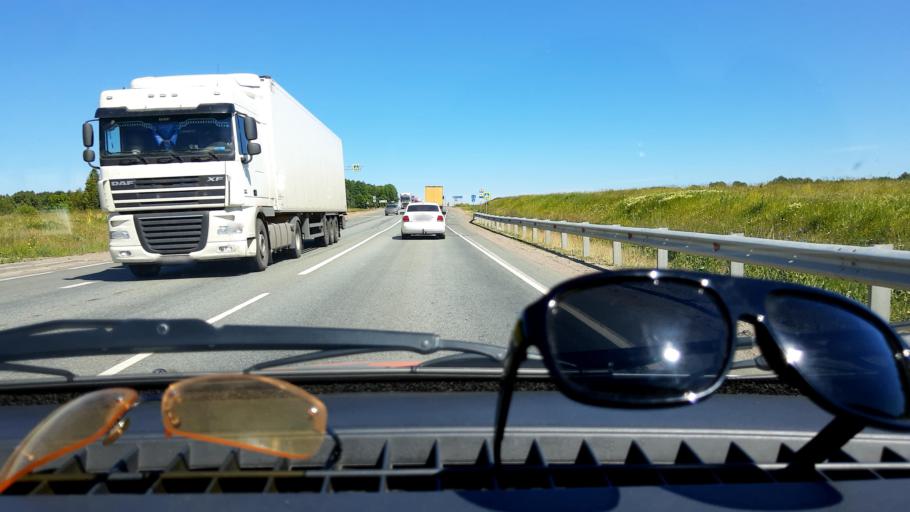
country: RU
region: Bashkortostan
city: Kudeyevskiy
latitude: 54.8173
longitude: 56.7896
